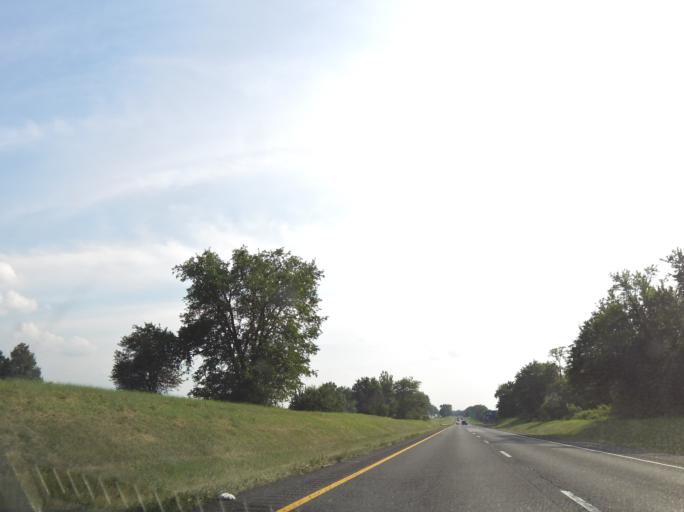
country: US
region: Maryland
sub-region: Washington County
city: Halfway
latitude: 39.6431
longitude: -77.7605
